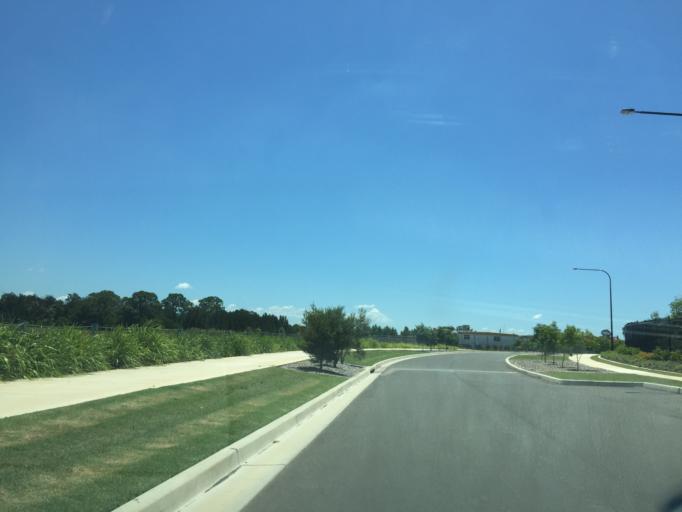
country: AU
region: New South Wales
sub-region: Blacktown
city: Doonside
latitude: -33.7943
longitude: 150.8635
